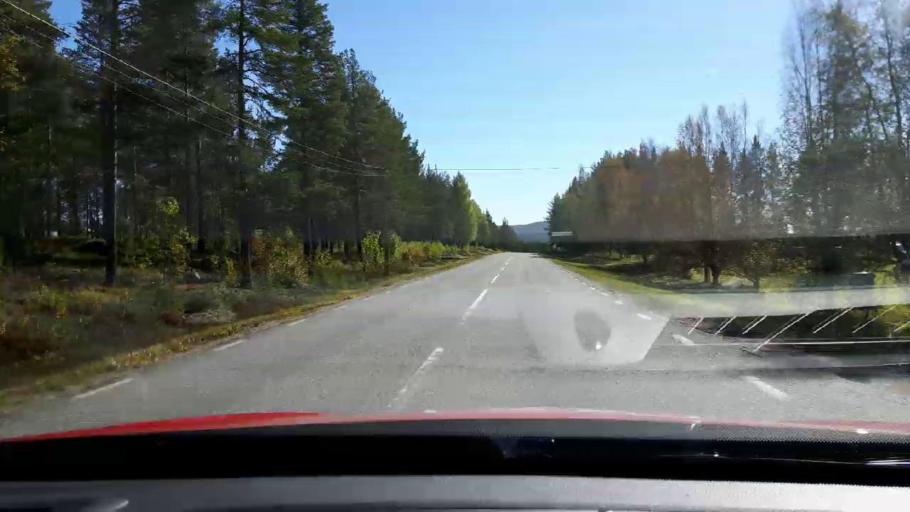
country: SE
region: Jaemtland
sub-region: Harjedalens Kommun
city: Sveg
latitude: 62.2989
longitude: 14.0692
